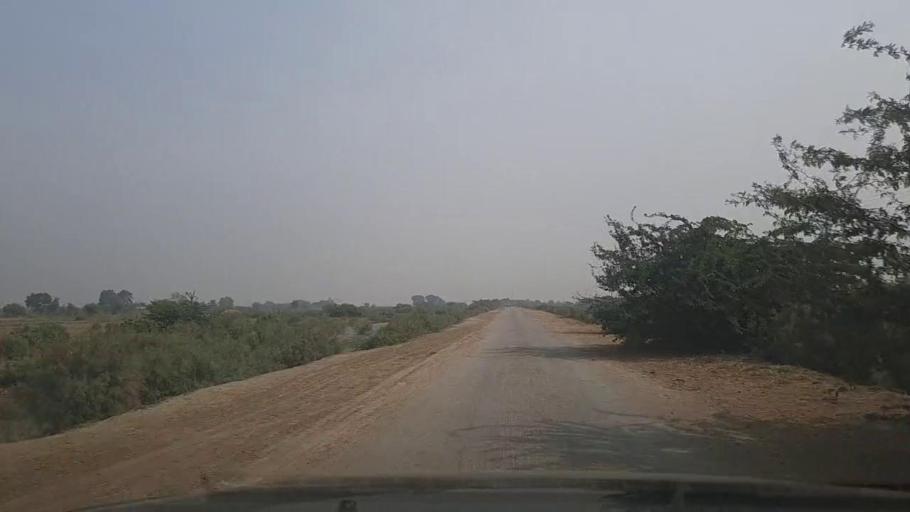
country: PK
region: Sindh
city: Mirpur Sakro
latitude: 24.4789
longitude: 67.6543
